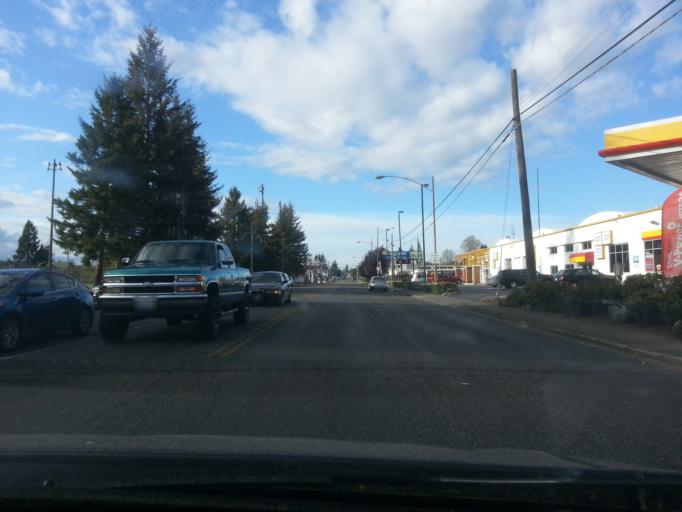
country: US
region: Washington
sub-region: Pierce County
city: Tacoma
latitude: 47.2466
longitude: -122.4629
